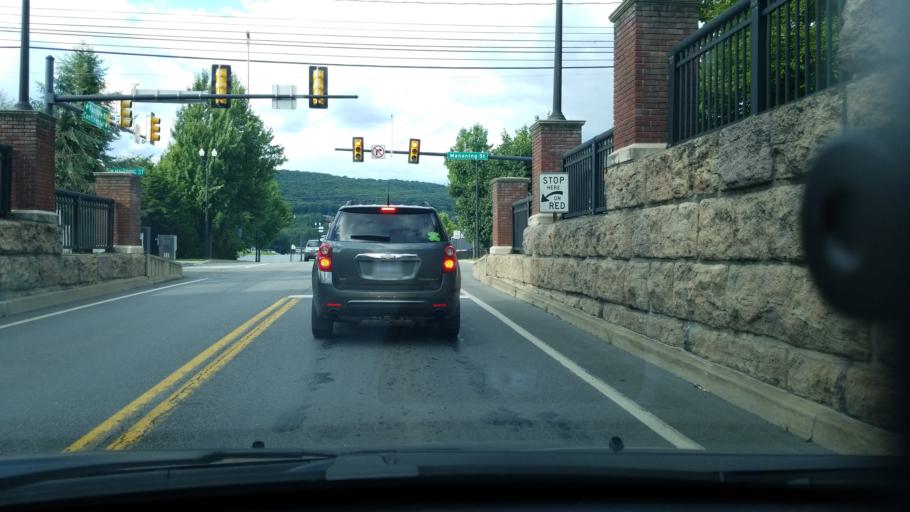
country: US
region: Pennsylvania
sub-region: Montour County
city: Danville
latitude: 40.9615
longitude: -76.6197
